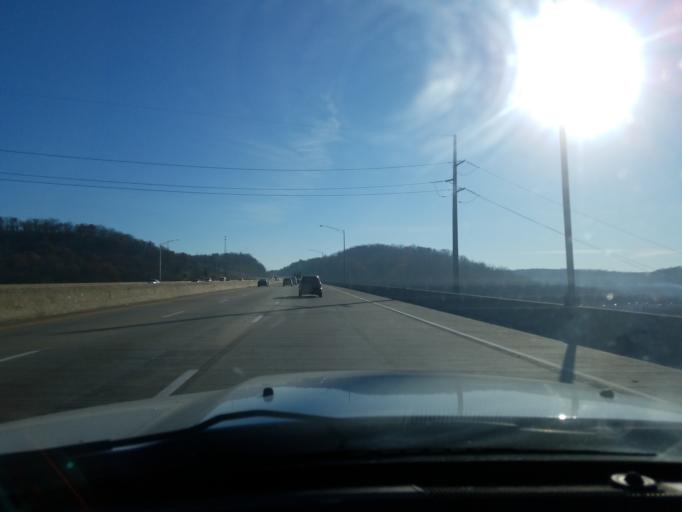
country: US
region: Kentucky
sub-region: Kenton County
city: Fort Wright
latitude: 39.0283
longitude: -84.5343
